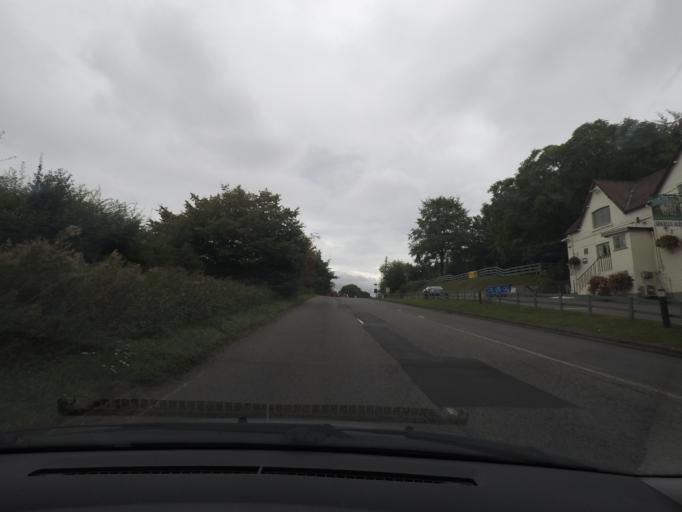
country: GB
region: England
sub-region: Borough of Swindon
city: Chiseldon
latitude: 51.5223
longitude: -1.7242
